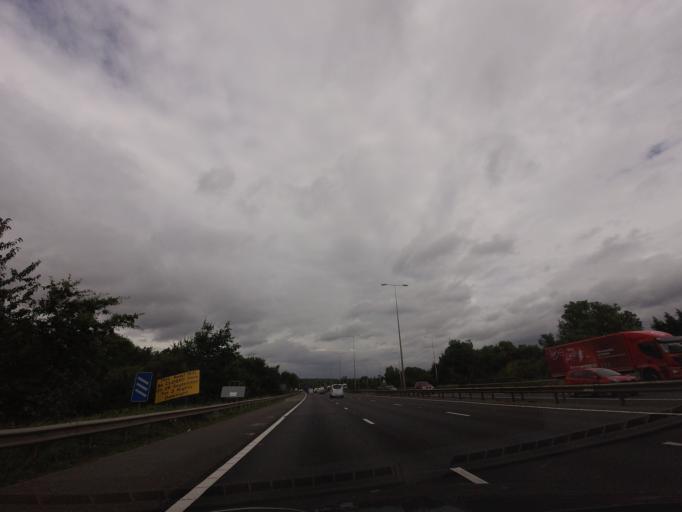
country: GB
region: England
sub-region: Leicestershire
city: Shepshed
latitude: 52.7526
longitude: -1.2748
